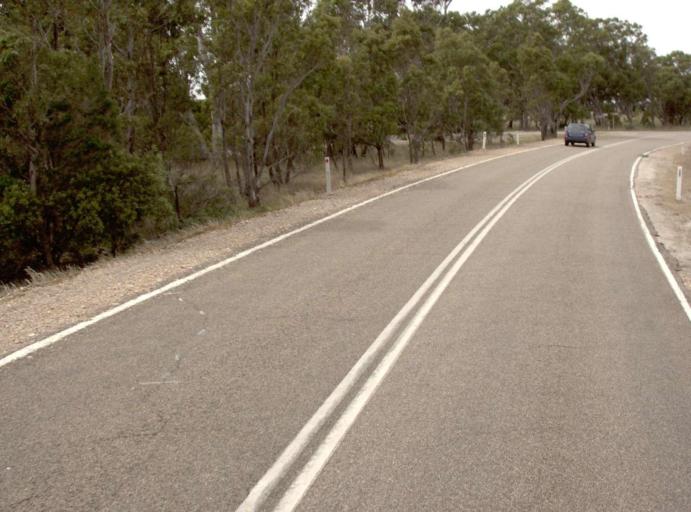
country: AU
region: Victoria
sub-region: Wellington
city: Sale
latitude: -37.9332
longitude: 147.0960
